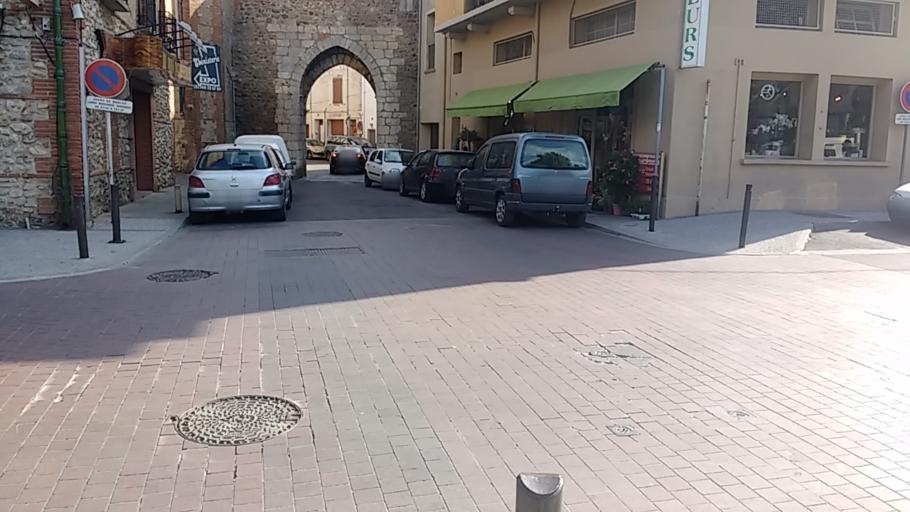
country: FR
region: Languedoc-Roussillon
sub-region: Departement des Pyrenees-Orientales
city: Elne
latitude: 42.6011
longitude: 2.9728
